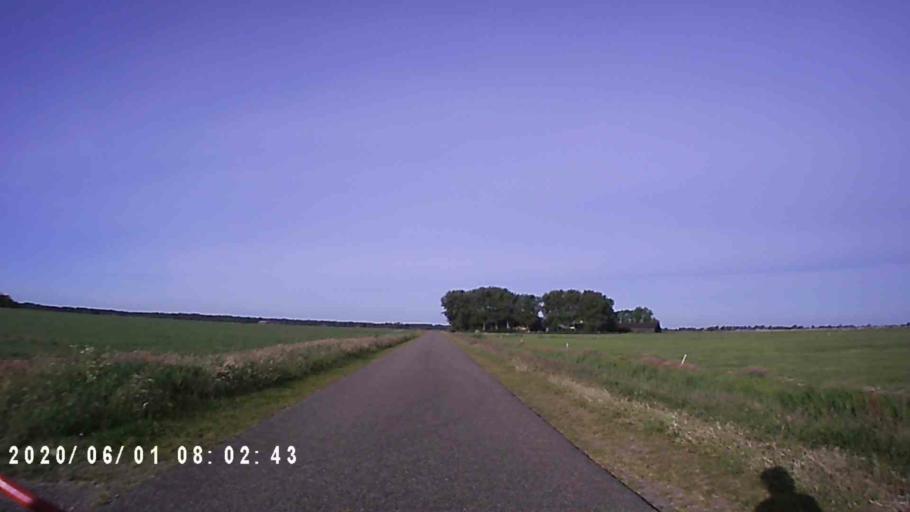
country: NL
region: Friesland
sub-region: Gemeente Dantumadiel
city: Rinsumageast
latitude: 53.2771
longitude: 5.9235
